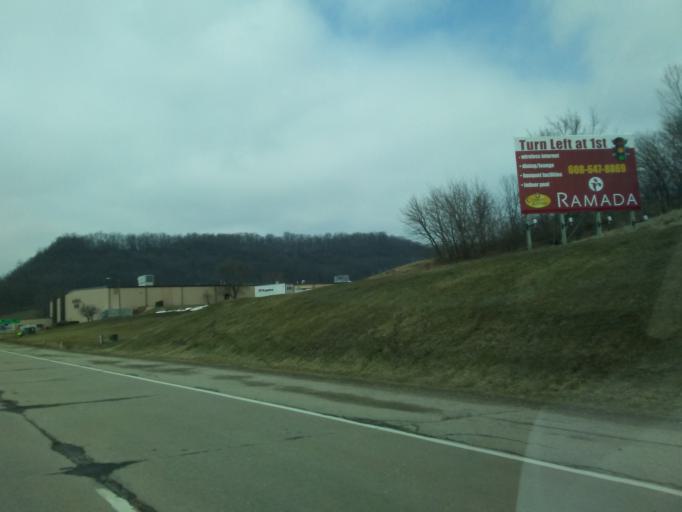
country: US
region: Wisconsin
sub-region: Richland County
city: Richland Center
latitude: 43.3197
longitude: -90.3687
